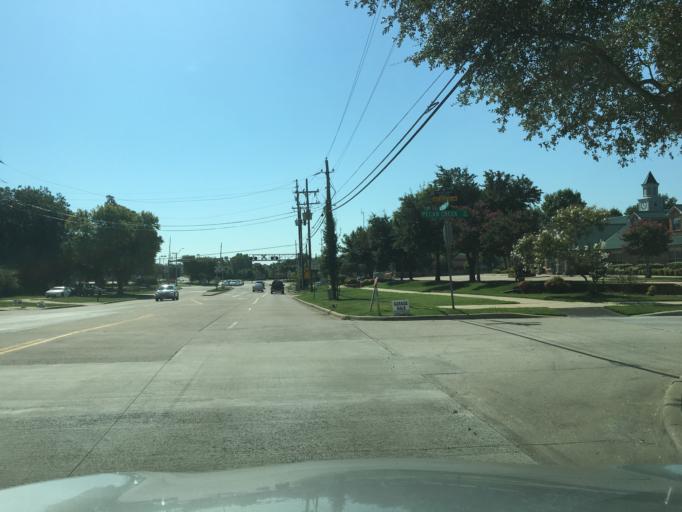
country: US
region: Texas
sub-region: Dallas County
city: Sachse
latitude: 32.9697
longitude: -96.6084
